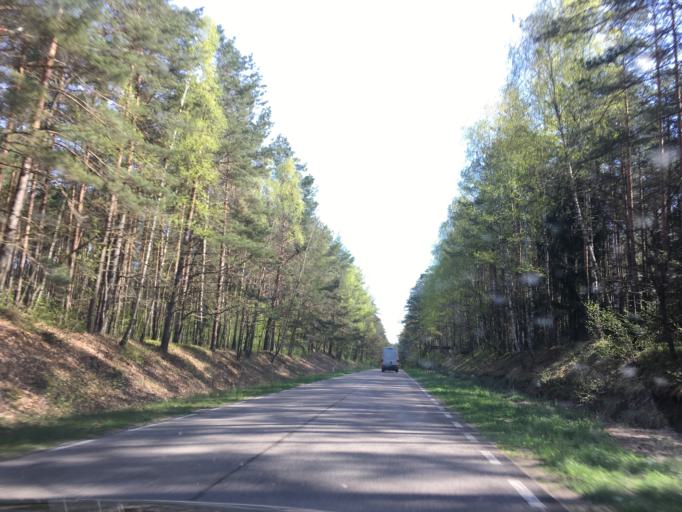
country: PL
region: Warmian-Masurian Voivodeship
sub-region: Powiat piski
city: Ruciane-Nida
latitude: 53.6736
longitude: 21.5804
